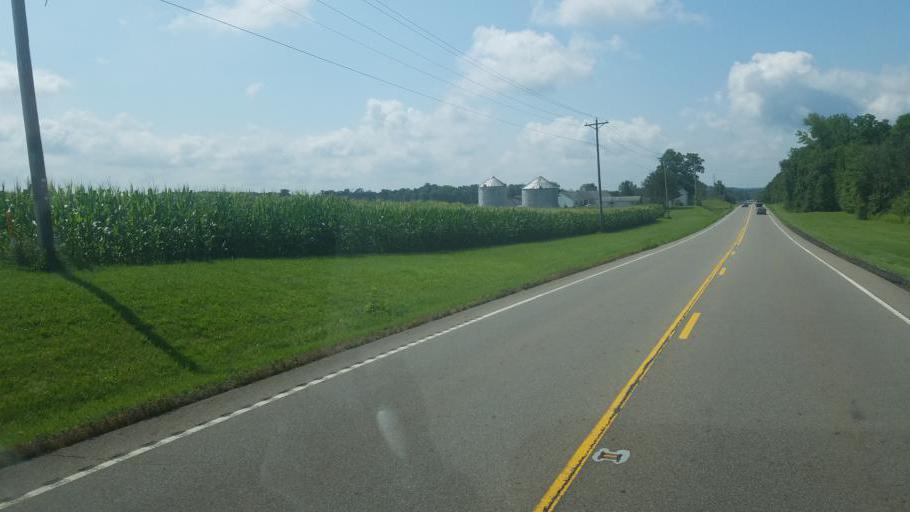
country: US
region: Ohio
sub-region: Licking County
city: Hebron
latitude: 39.9999
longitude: -82.5243
